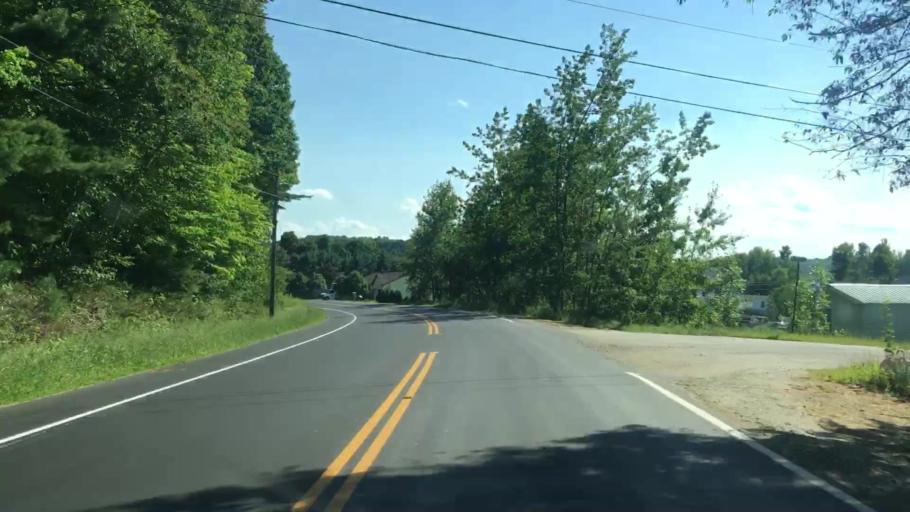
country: US
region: Maine
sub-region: Androscoggin County
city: Sabattus
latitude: 44.1318
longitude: -70.0877
